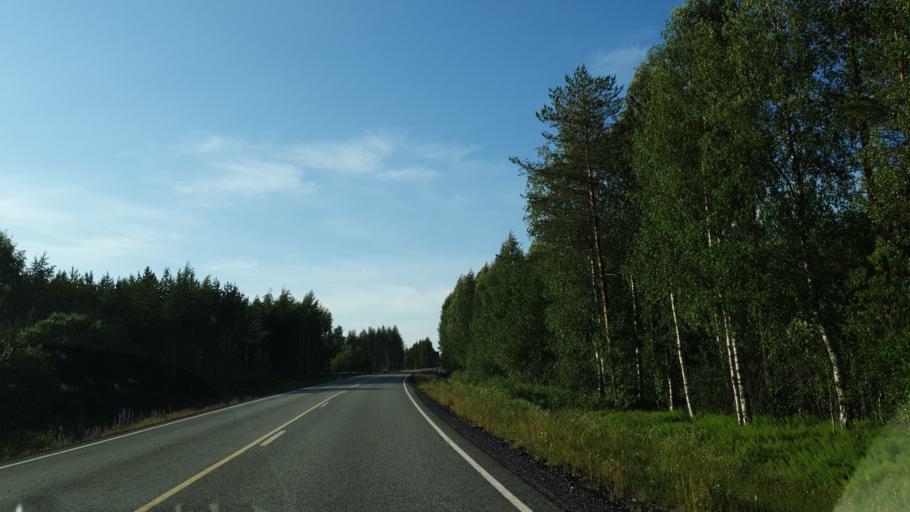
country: FI
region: Kainuu
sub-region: Kehys-Kainuu
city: Kuhmo
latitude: 64.0789
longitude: 29.4869
